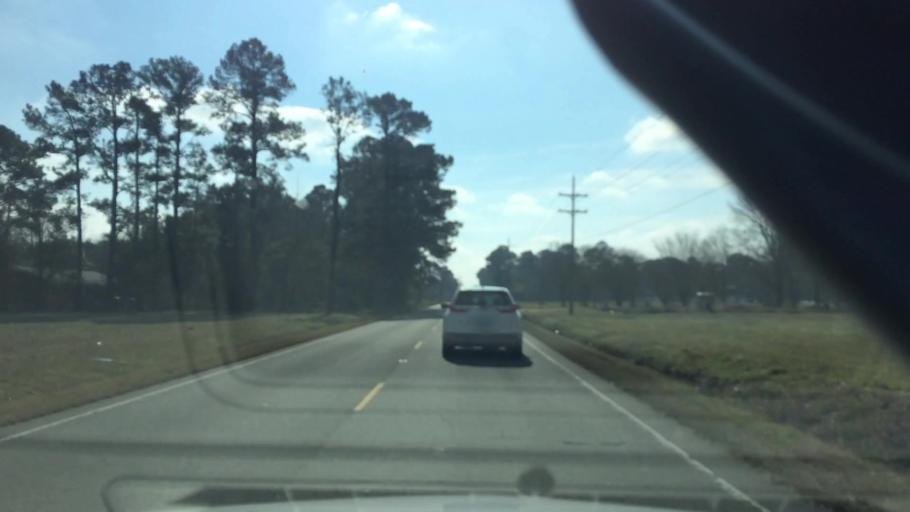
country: US
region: North Carolina
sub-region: Duplin County
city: Beulaville
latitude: 34.9019
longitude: -77.7799
